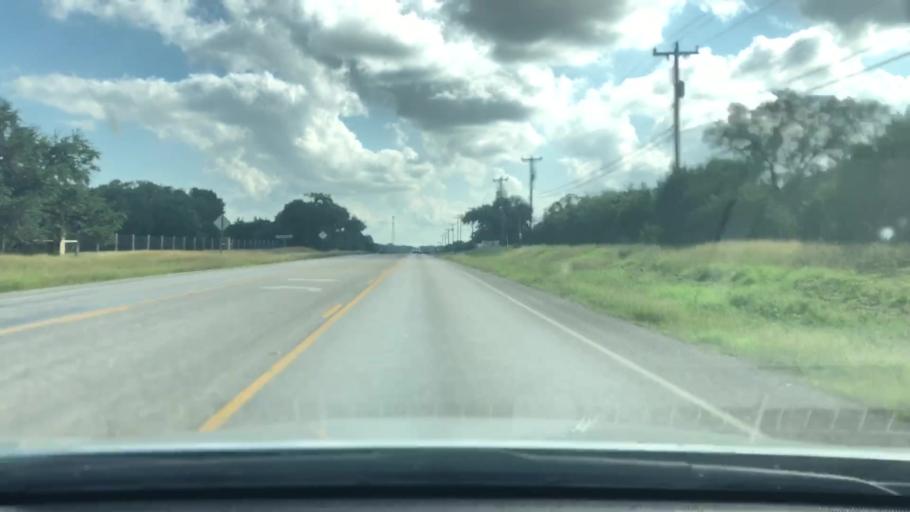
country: US
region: Texas
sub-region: Bexar County
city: Fair Oaks Ranch
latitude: 29.7514
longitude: -98.6235
